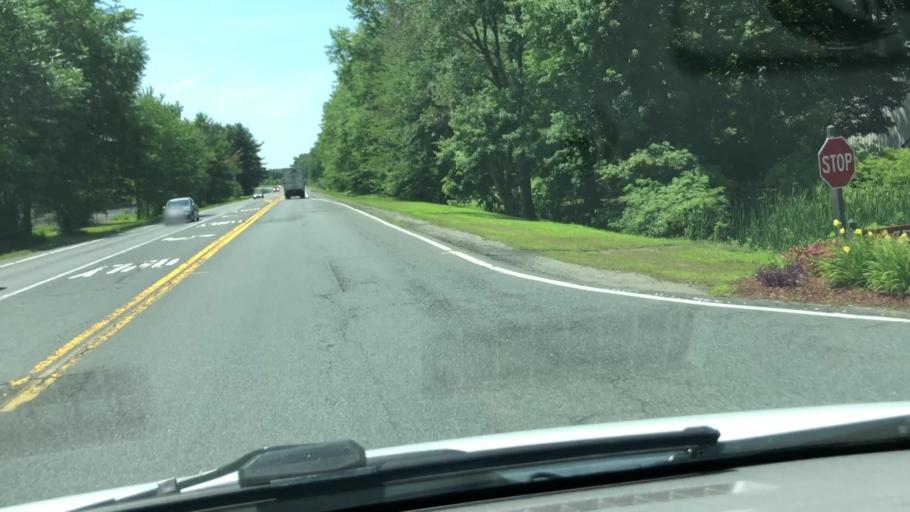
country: US
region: Massachusetts
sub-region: Franklin County
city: South Deerfield
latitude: 42.4746
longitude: -72.6141
